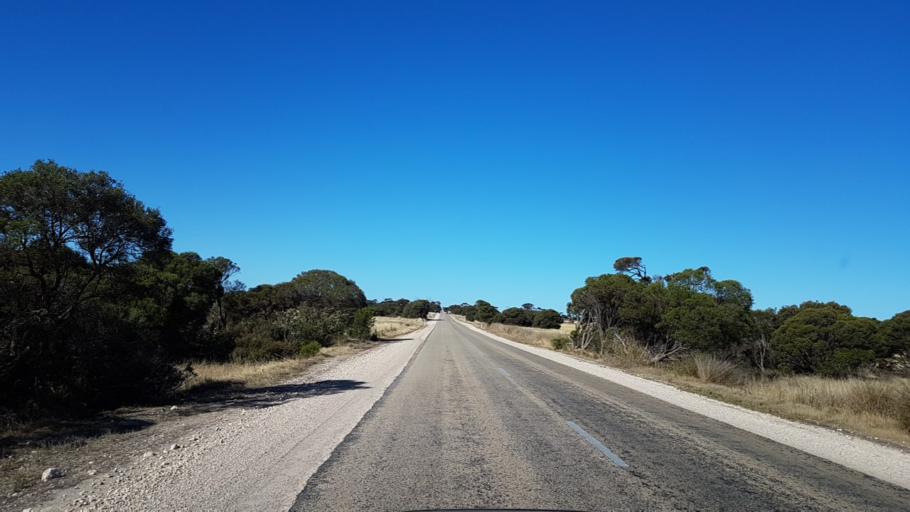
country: AU
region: South Australia
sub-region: Yorke Peninsula
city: Port Victoria
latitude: -34.6878
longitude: 137.7040
